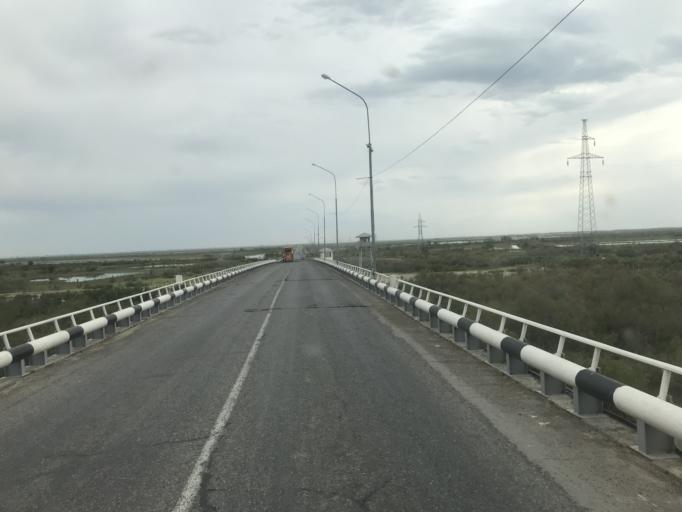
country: KZ
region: Ongtustik Qazaqstan
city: Ilyich
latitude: 41.0291
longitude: 68.5171
